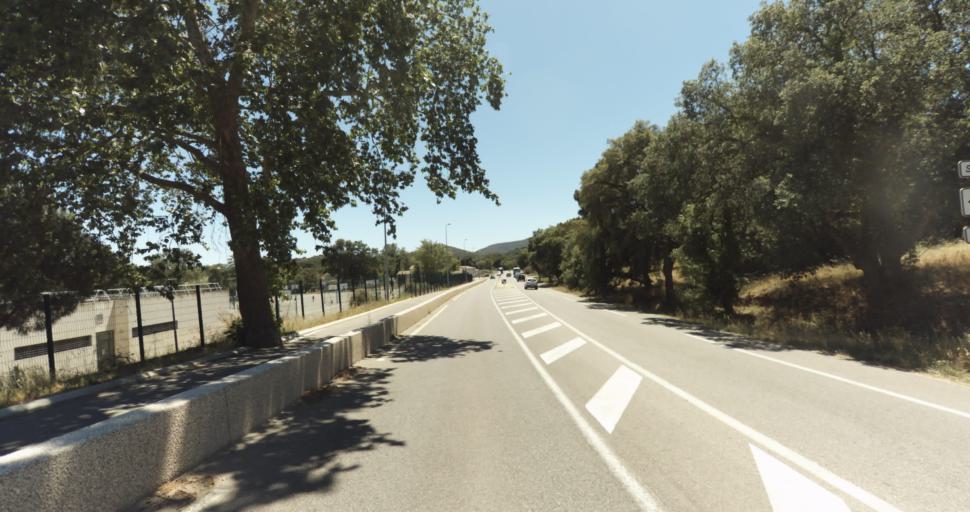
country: FR
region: Provence-Alpes-Cote d'Azur
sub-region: Departement du Var
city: Gassin
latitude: 43.2471
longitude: 6.5721
